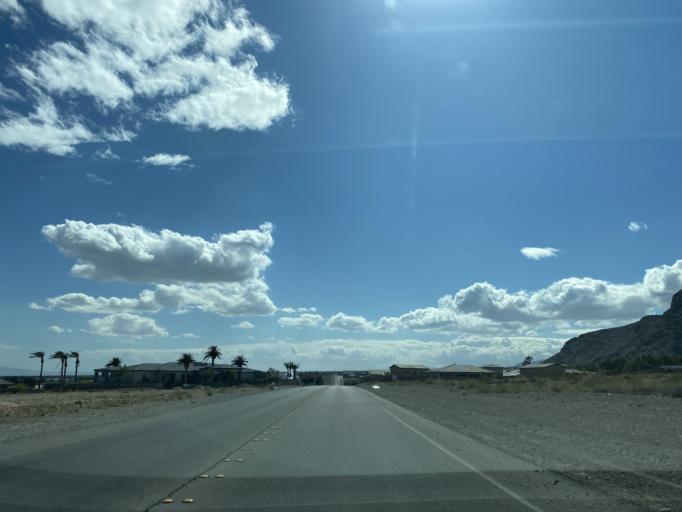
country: US
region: Nevada
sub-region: Clark County
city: Summerlin South
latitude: 36.2457
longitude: -115.3063
